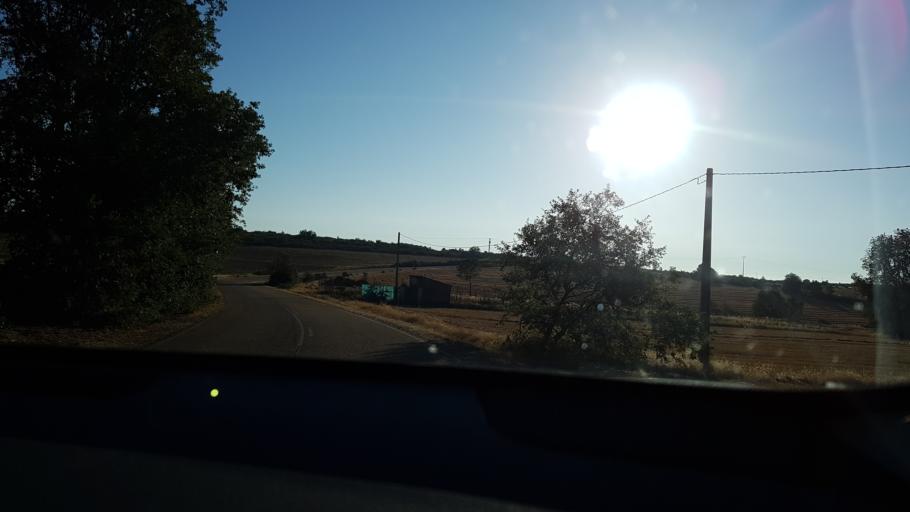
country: ES
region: Castille and Leon
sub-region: Provincia de Zamora
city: Samir de los Canos
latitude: 41.6623
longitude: -6.1841
